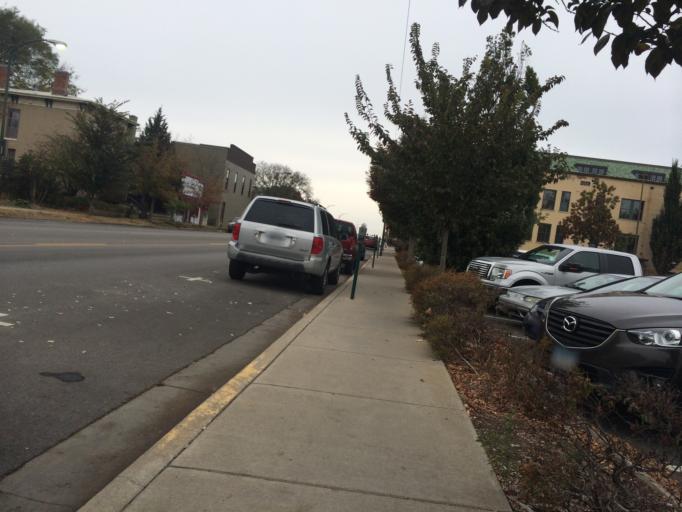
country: US
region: Kansas
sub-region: Douglas County
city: Lawrence
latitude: 38.9685
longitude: -95.2370
